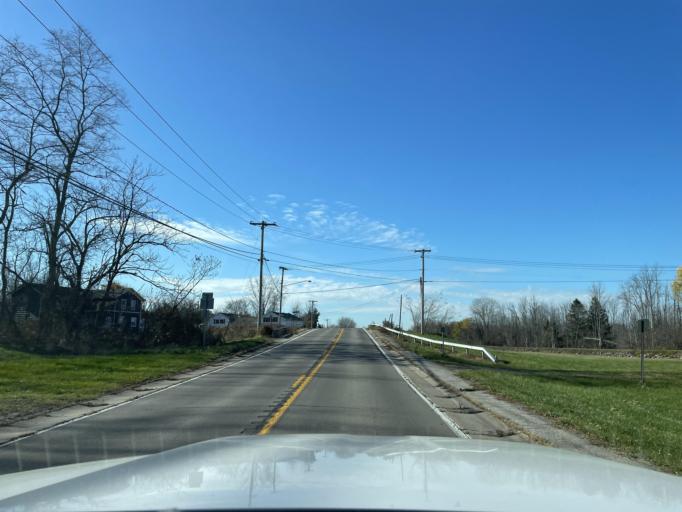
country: US
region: New York
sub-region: Orleans County
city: Medina
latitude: 43.2163
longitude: -78.4297
